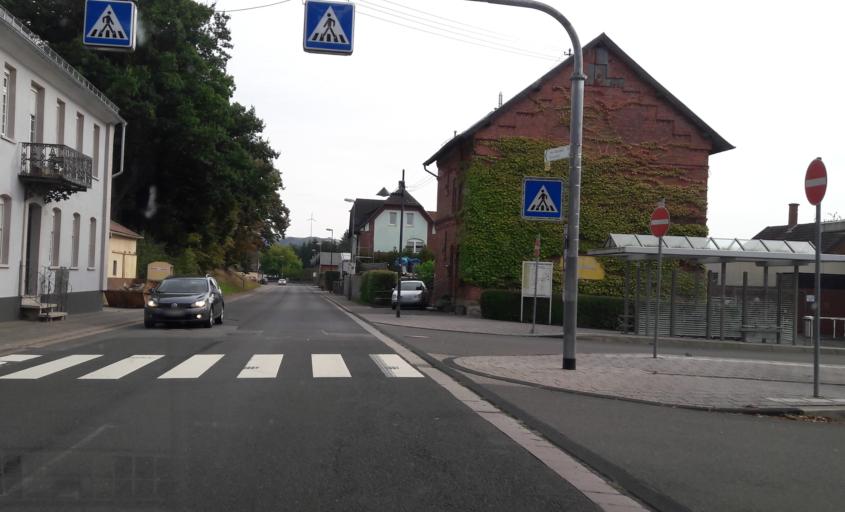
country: DE
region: Rheinland-Pfalz
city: Ellweiler
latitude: 49.6064
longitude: 7.1720
